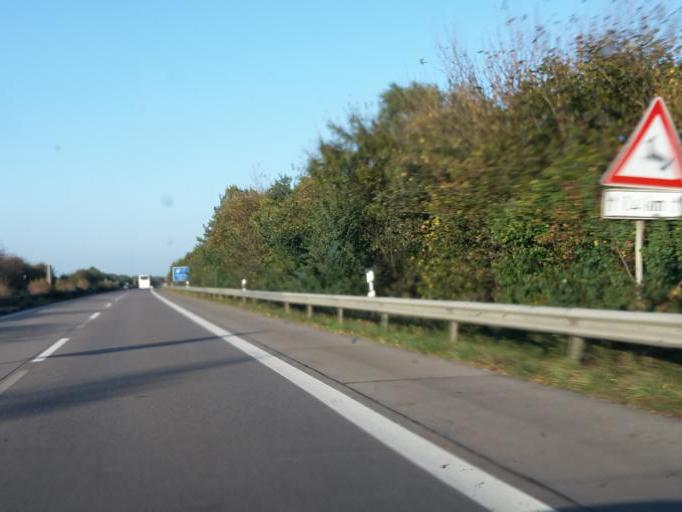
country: DE
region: Lower Saxony
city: Wardenburg
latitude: 53.0490
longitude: 8.2238
